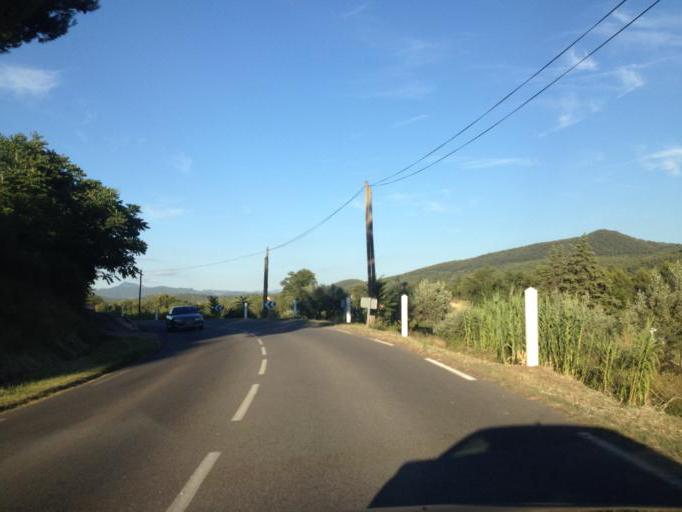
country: FR
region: Provence-Alpes-Cote d'Azur
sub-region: Departement du Vaucluse
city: Sablet
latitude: 44.2374
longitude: 5.0064
